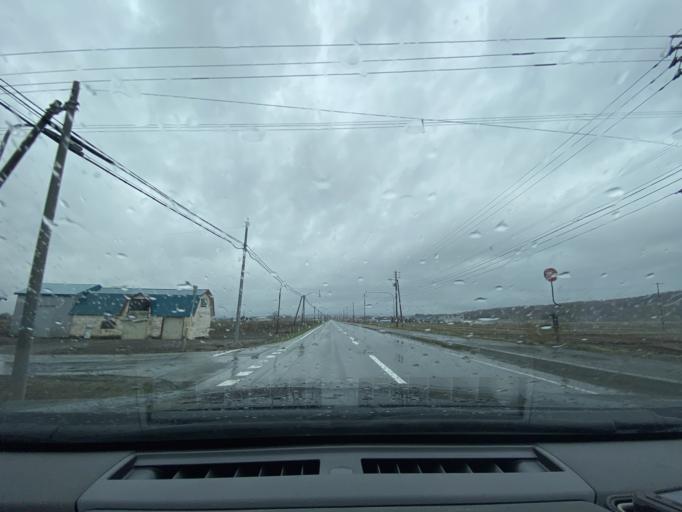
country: JP
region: Hokkaido
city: Fukagawa
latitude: 43.8143
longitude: 141.9709
